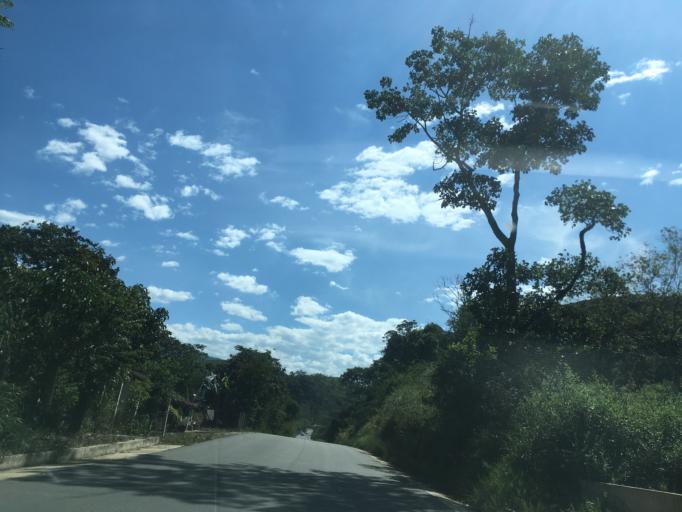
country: CO
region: Santander
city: Coromoro
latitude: 6.2978
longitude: -73.1464
